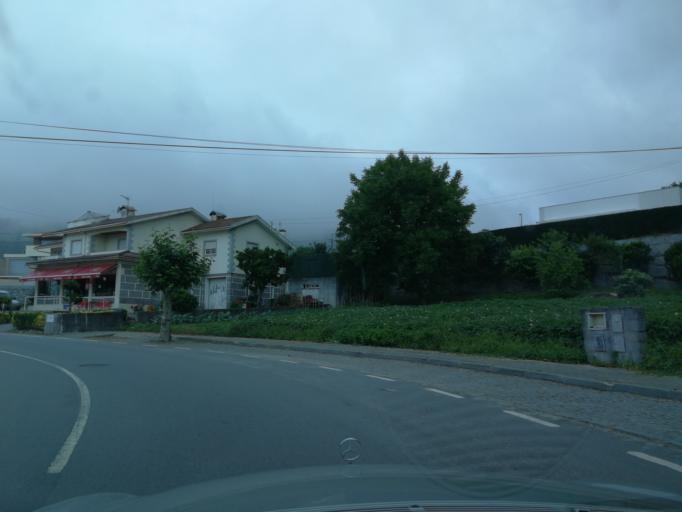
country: PT
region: Braga
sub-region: Guimaraes
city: Ponte
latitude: 41.5208
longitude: -8.3612
